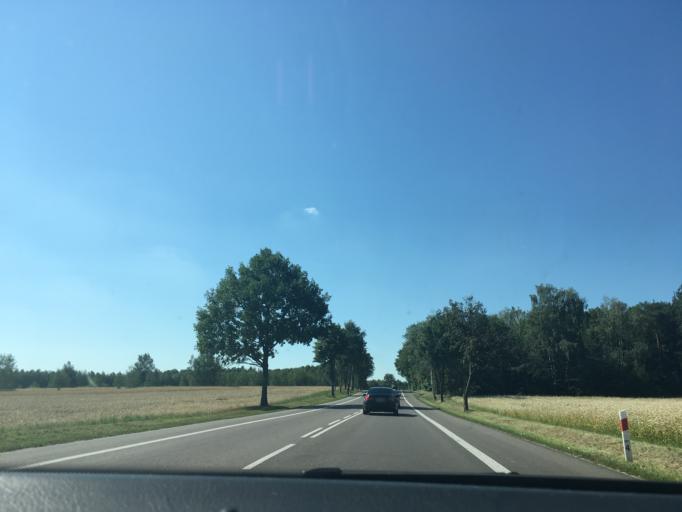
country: PL
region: Lublin Voivodeship
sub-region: Powiat lubartowski
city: Serniki
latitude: 51.4069
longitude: 22.6383
